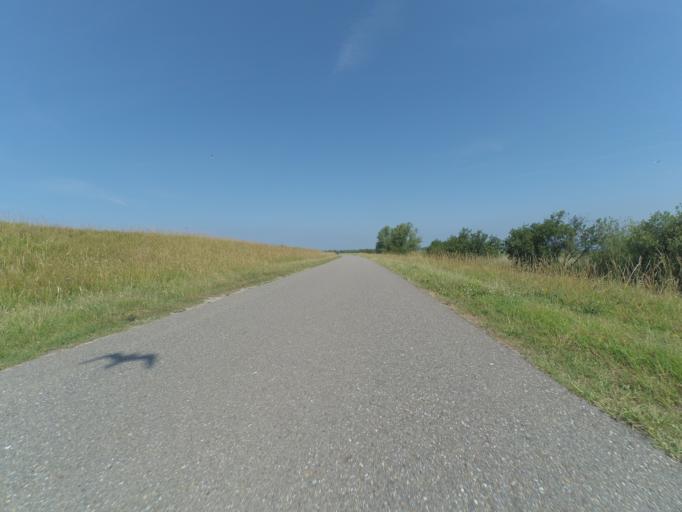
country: NL
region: North Brabant
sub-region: Gemeente Steenbergen
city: Nieuw-Vossemeer
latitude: 51.6450
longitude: 4.1899
